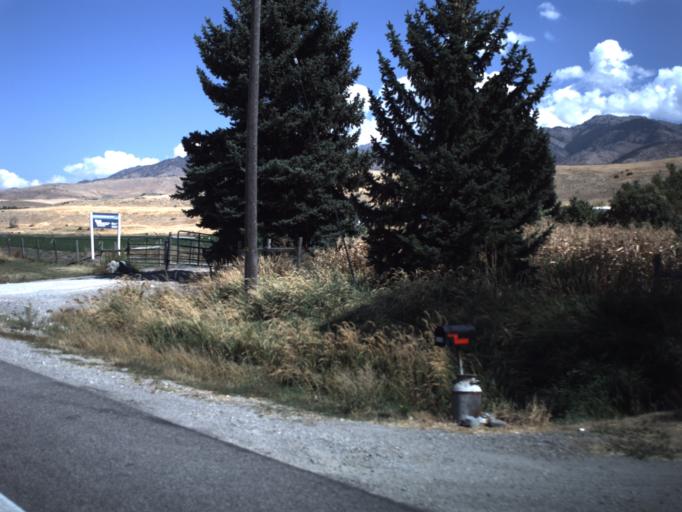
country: US
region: Utah
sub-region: Cache County
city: Richmond
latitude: 41.8891
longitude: -111.8156
